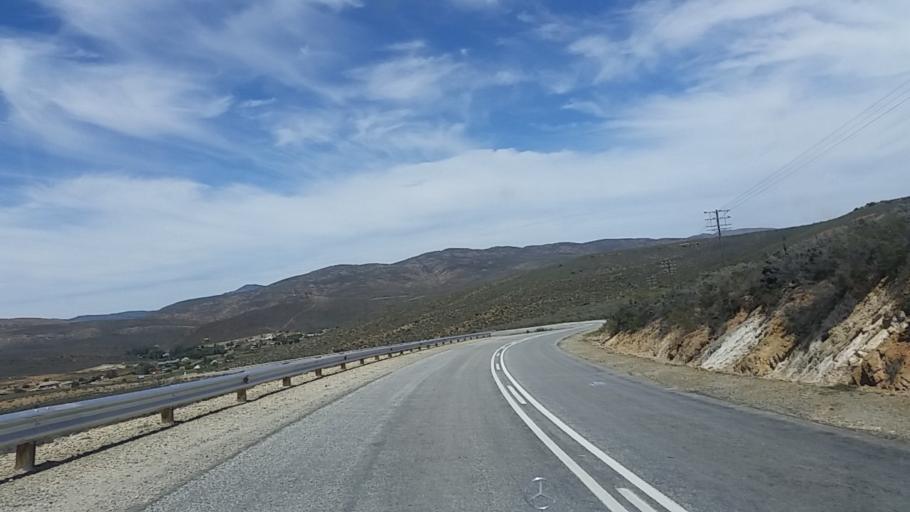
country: ZA
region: Western Cape
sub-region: Eden District Municipality
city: Knysna
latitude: -33.6366
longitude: 23.1300
